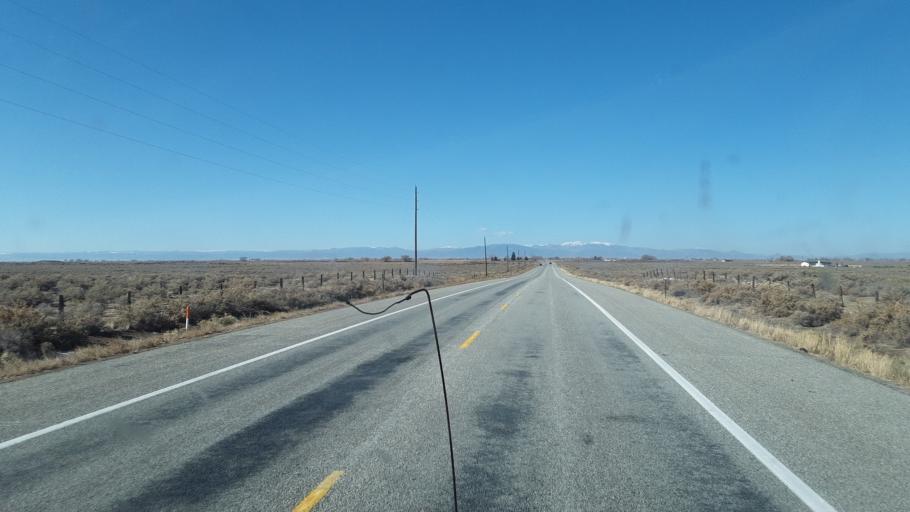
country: US
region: Colorado
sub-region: Alamosa County
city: Alamosa East
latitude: 37.4742
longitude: -105.7395
